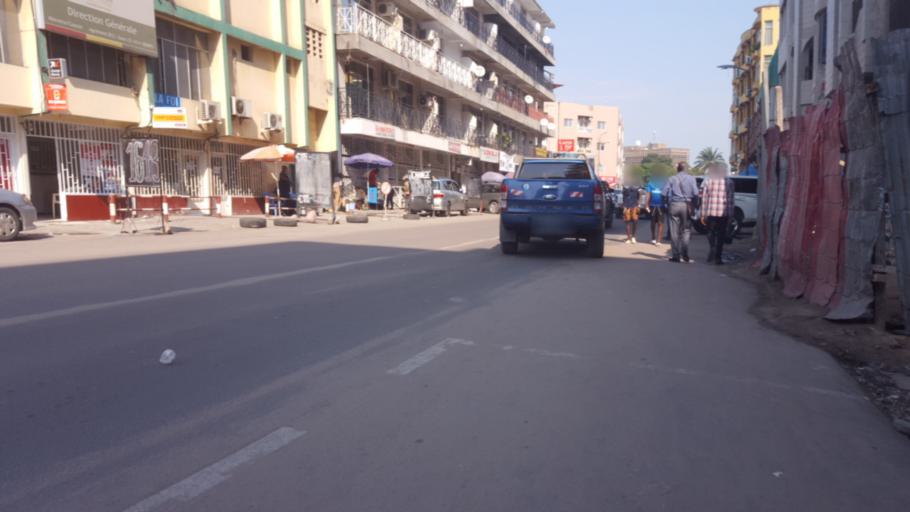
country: CD
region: Kinshasa
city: Kinshasa
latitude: -4.3056
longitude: 15.3063
